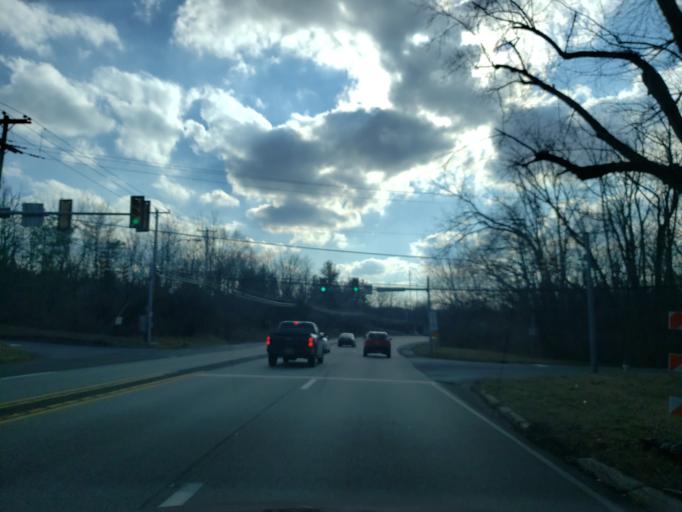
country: US
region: Pennsylvania
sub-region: Montgomery County
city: North Wales
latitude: 40.1939
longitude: -75.2603
